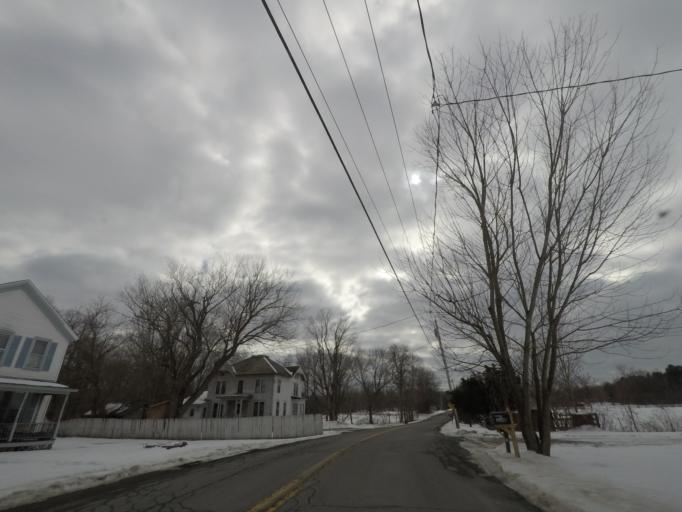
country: US
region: New York
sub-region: Washington County
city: Cambridge
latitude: 42.9521
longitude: -73.4333
